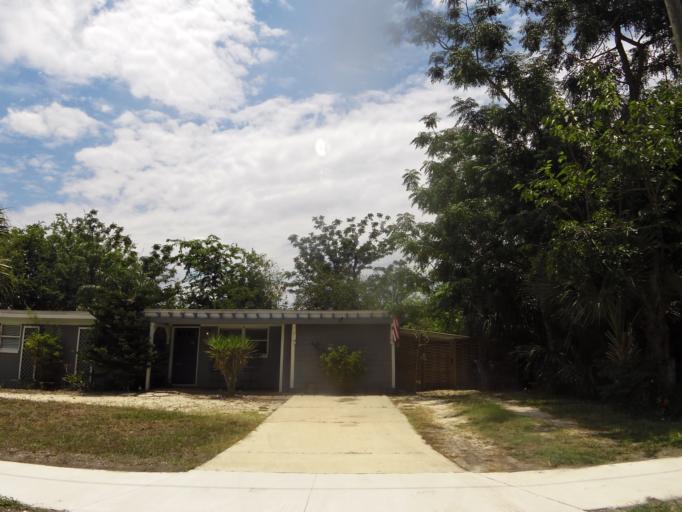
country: US
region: Florida
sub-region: Duval County
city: Atlantic Beach
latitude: 30.3320
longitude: -81.4127
